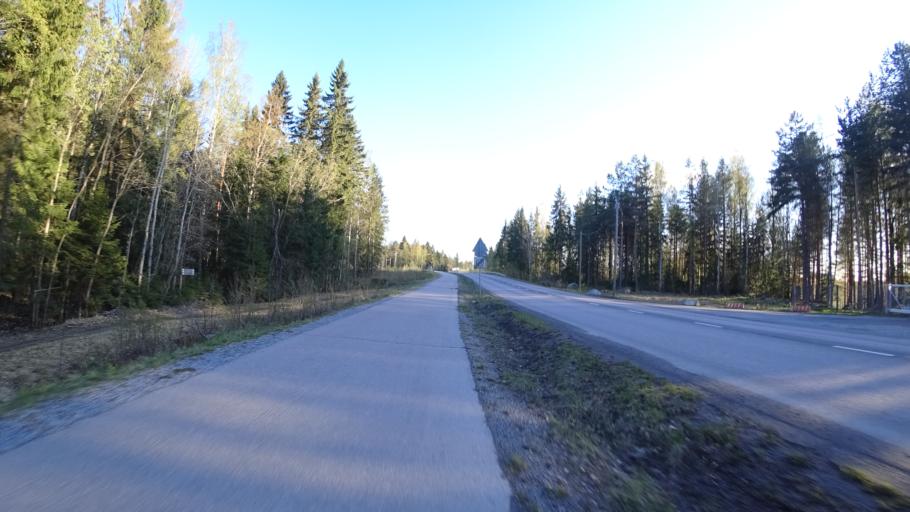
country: FI
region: Pirkanmaa
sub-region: Tampere
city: Nokia
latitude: 61.4929
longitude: 23.5340
